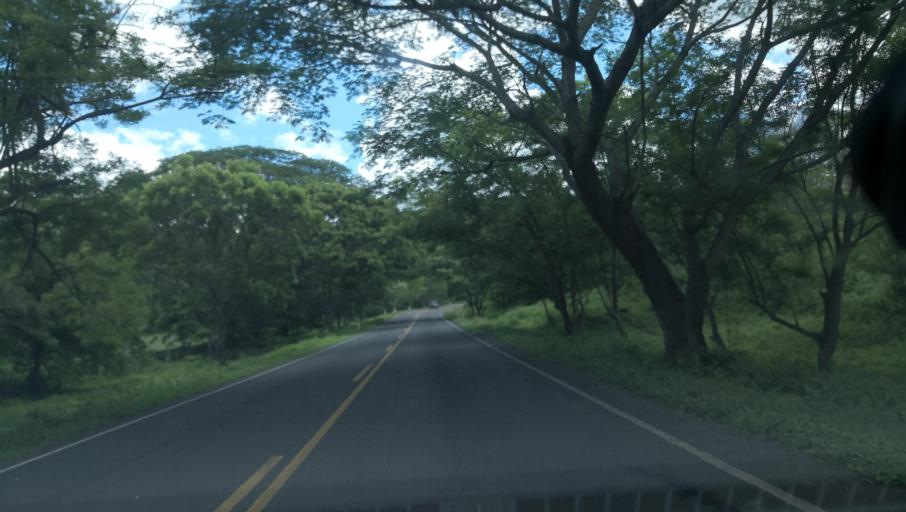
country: NI
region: Madriz
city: Palacaguina
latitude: 13.4337
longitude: -86.4232
